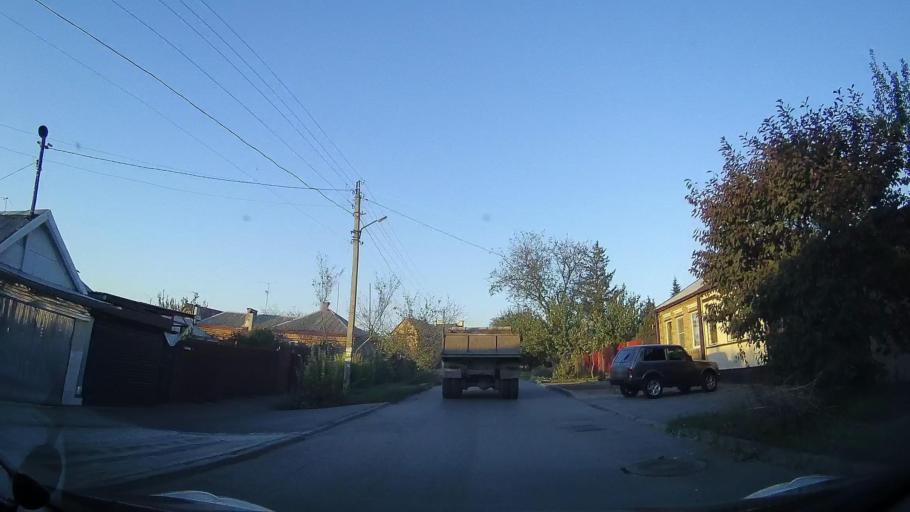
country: RU
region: Rostov
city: Rostov-na-Donu
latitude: 47.2514
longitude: 39.6839
